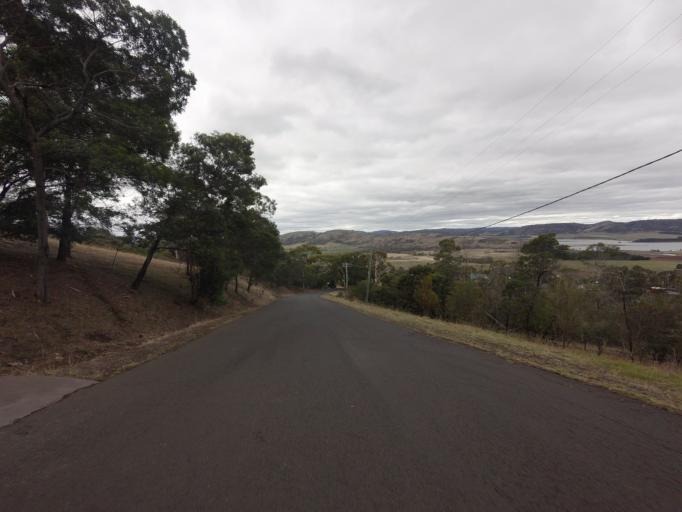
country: AU
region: Tasmania
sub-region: Clarence
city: Cambridge
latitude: -42.7887
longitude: 147.4097
